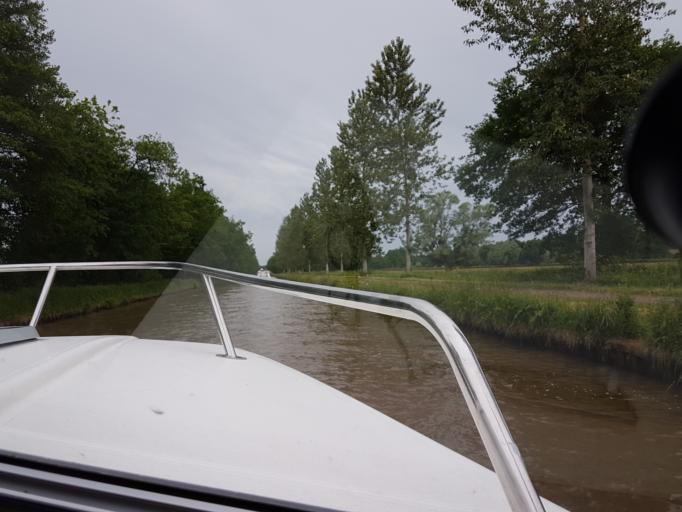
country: FR
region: Bourgogne
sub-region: Departement de la Nievre
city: Clamecy
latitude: 47.3863
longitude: 3.6002
